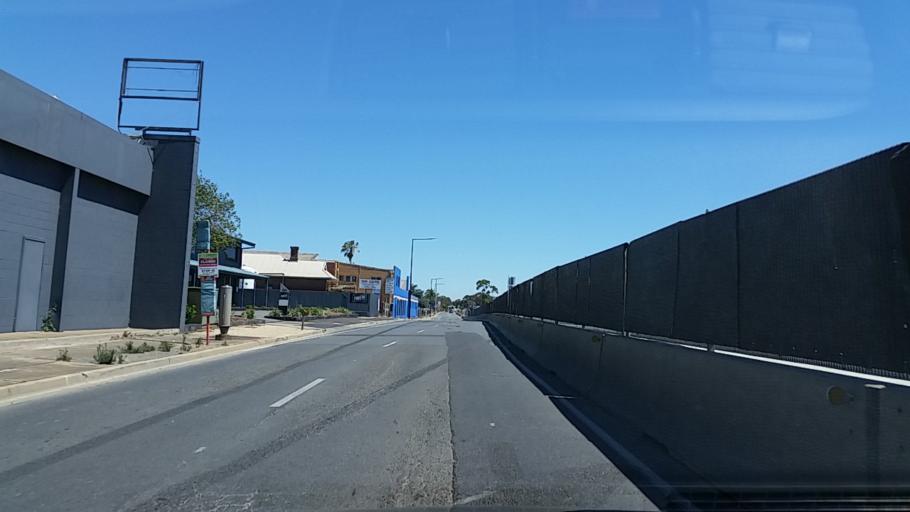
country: AU
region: South Australia
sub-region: City of West Torrens
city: Thebarton
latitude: -34.9049
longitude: 138.5658
